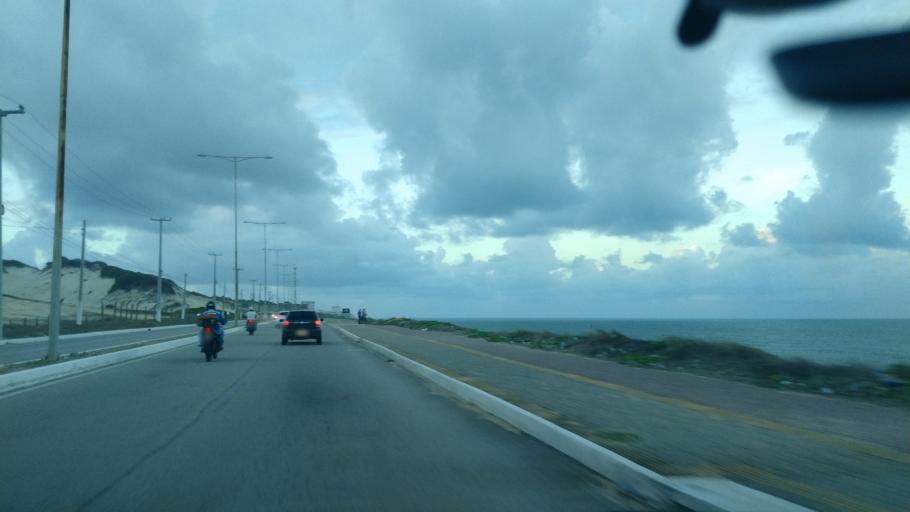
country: BR
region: Rio Grande do Norte
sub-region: Natal
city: Natal
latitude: -5.8517
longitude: -35.1822
